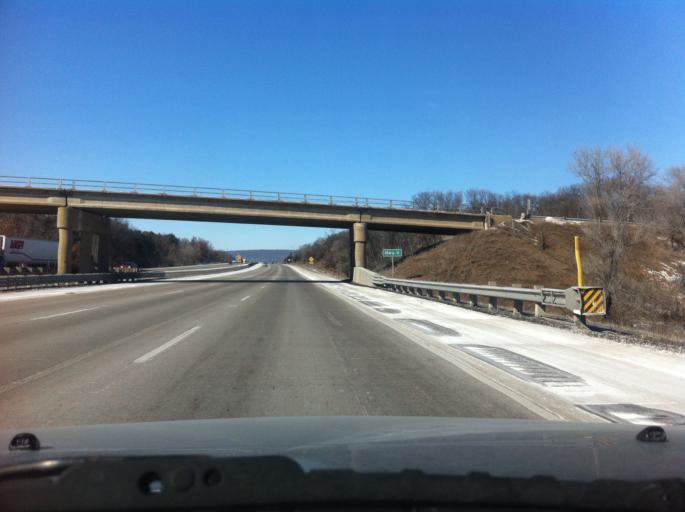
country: US
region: Wisconsin
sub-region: Columbia County
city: Poynette
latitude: 43.4210
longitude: -89.4750
